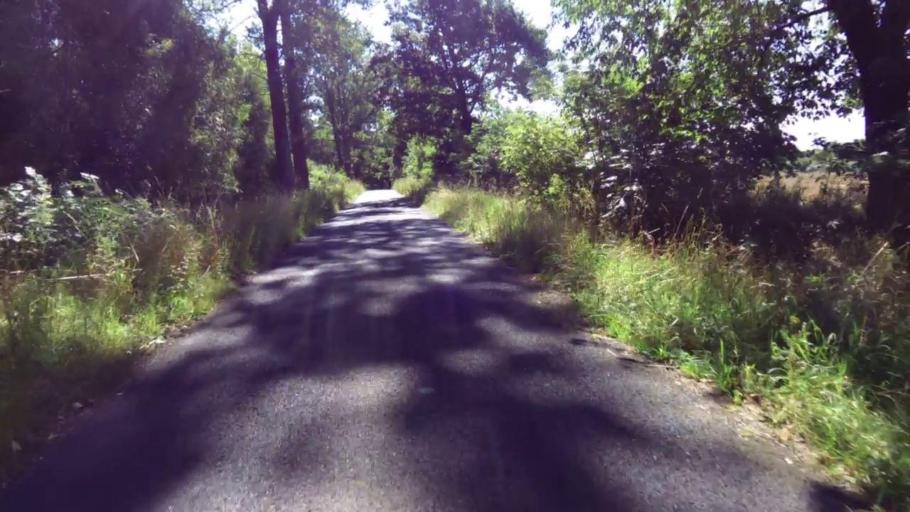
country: PL
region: West Pomeranian Voivodeship
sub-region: Powiat drawski
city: Wierzchowo
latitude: 53.5295
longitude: 16.0826
